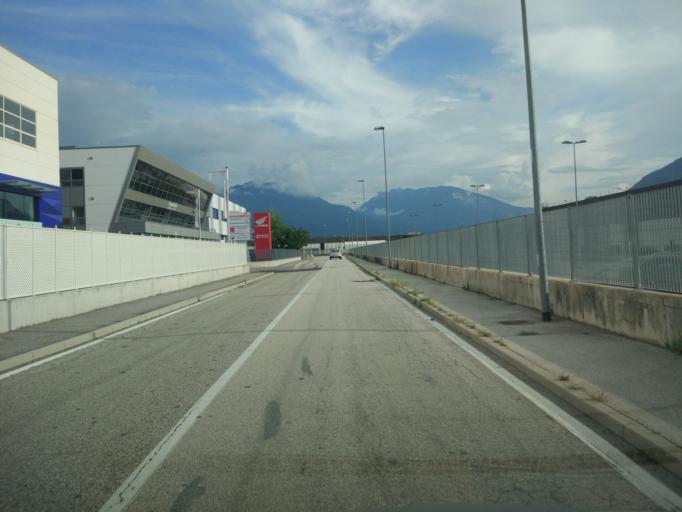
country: IT
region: Trentino-Alto Adige
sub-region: Provincia di Trento
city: Meano
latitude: 46.1173
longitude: 11.0971
